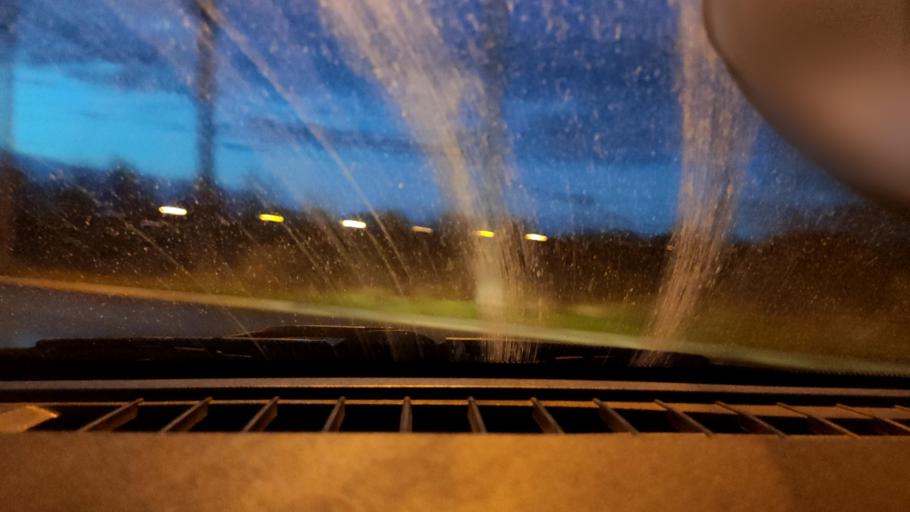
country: RU
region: Perm
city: Kondratovo
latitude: 58.0022
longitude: 56.1053
